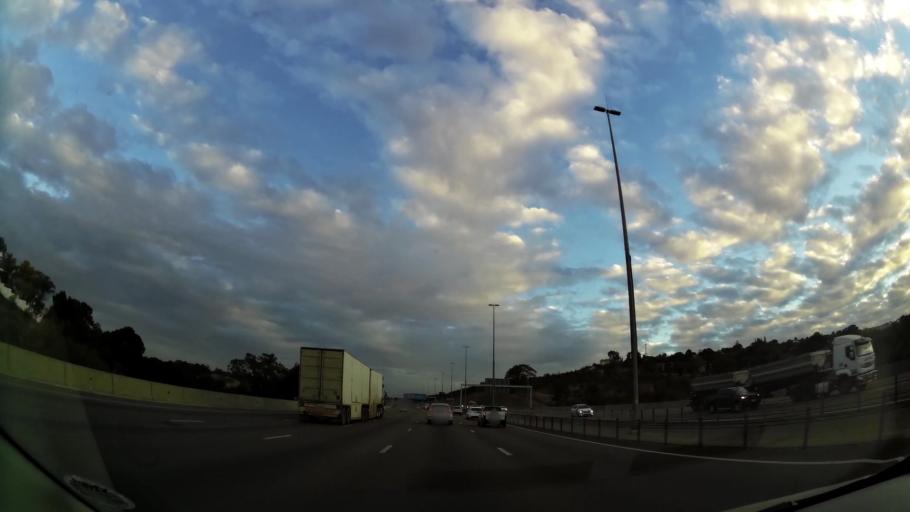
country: ZA
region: Gauteng
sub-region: City of Tshwane Metropolitan Municipality
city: Pretoria
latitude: -25.7985
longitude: 28.2636
